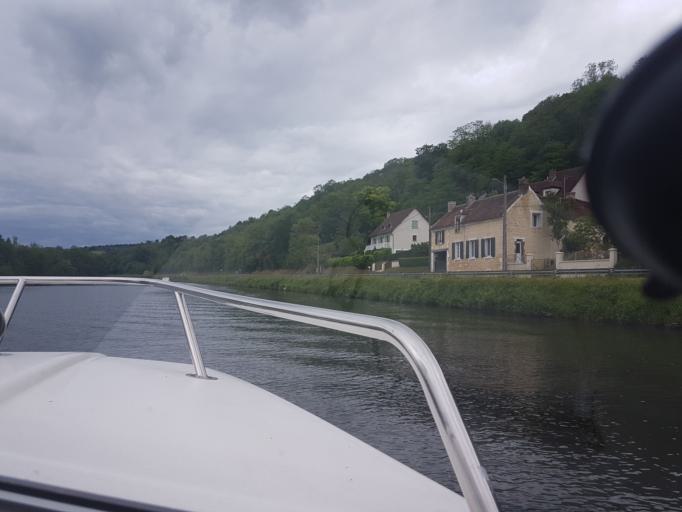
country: FR
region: Bourgogne
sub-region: Departement de l'Yonne
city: Champs-sur-Yonne
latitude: 47.7516
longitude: 3.5889
